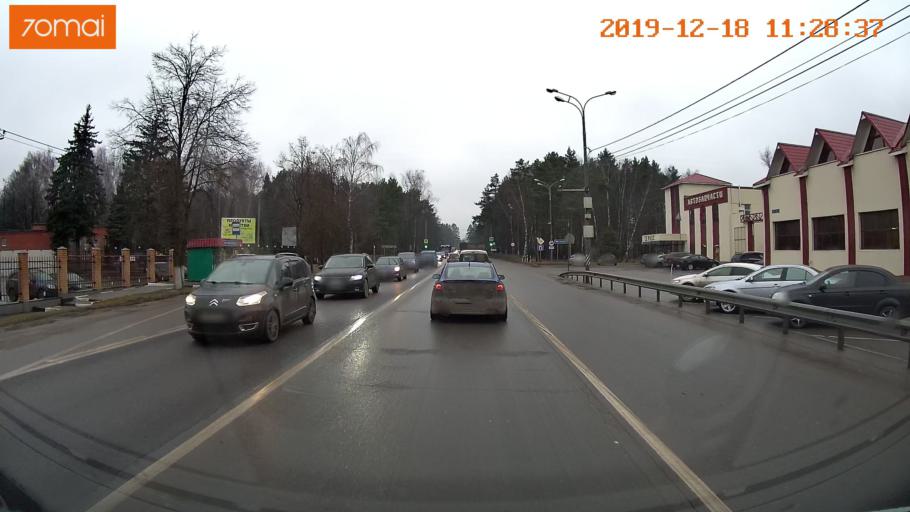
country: RU
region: Moskovskaya
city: Bol'shiye Vyazemy
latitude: 55.6442
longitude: 36.9774
